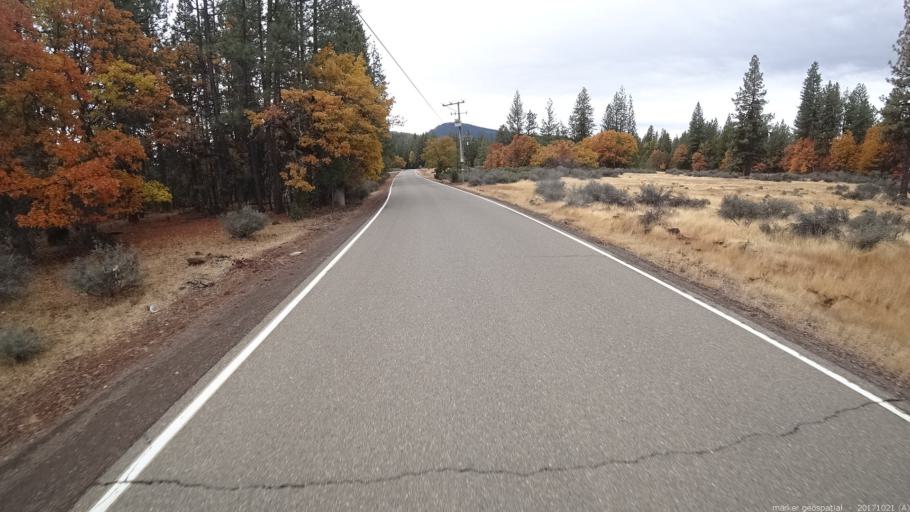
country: US
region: California
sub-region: Shasta County
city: Burney
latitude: 41.0321
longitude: -121.6717
